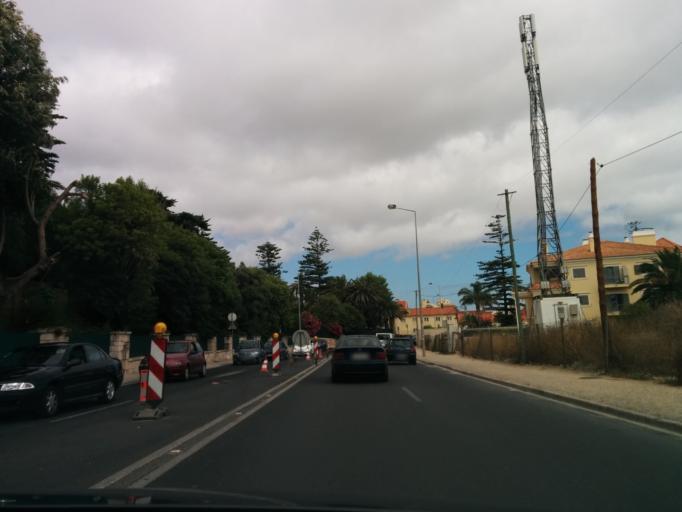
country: PT
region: Lisbon
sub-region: Cascais
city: Estoril
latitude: 38.7045
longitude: -9.4043
